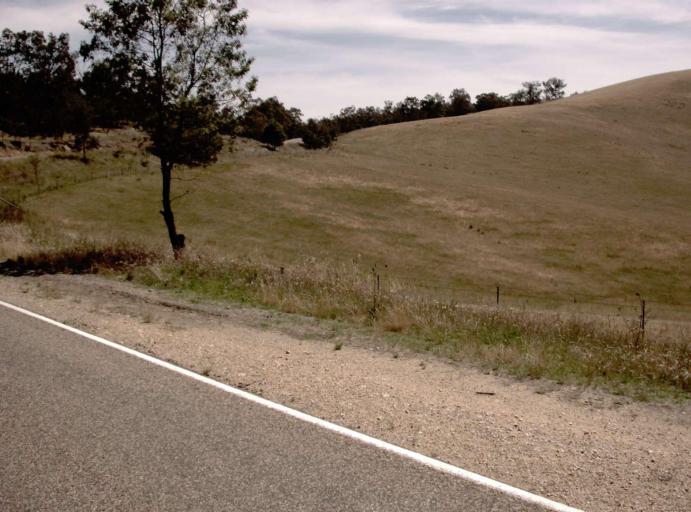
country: AU
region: Victoria
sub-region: Alpine
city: Mount Beauty
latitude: -37.0543
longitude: 147.6169
